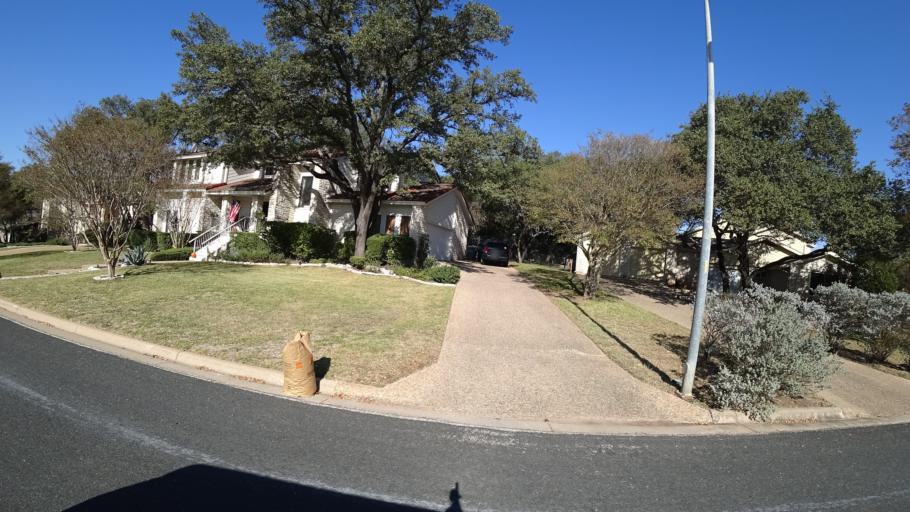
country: US
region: Texas
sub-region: Williamson County
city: Jollyville
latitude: 30.4074
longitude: -97.7633
